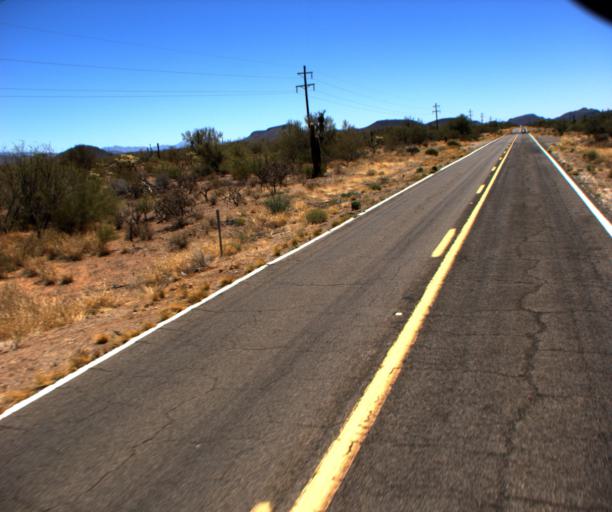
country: US
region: Arizona
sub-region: Pima County
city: Sells
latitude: 32.0173
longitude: -111.9991
